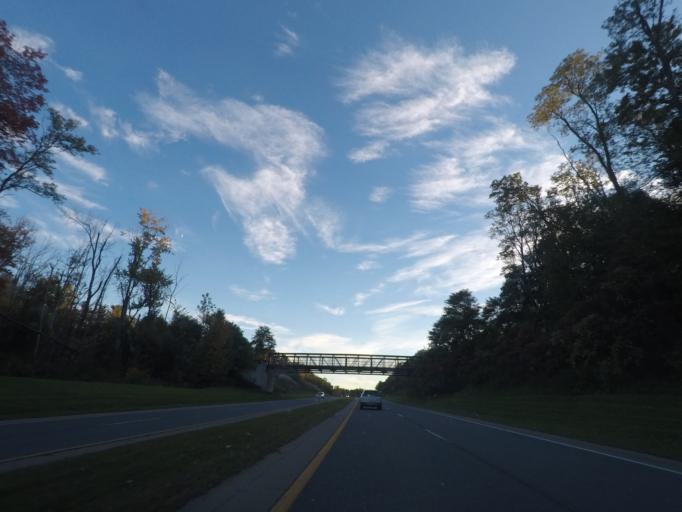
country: US
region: New York
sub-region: Albany County
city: Colonie
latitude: 42.7440
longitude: -73.8182
